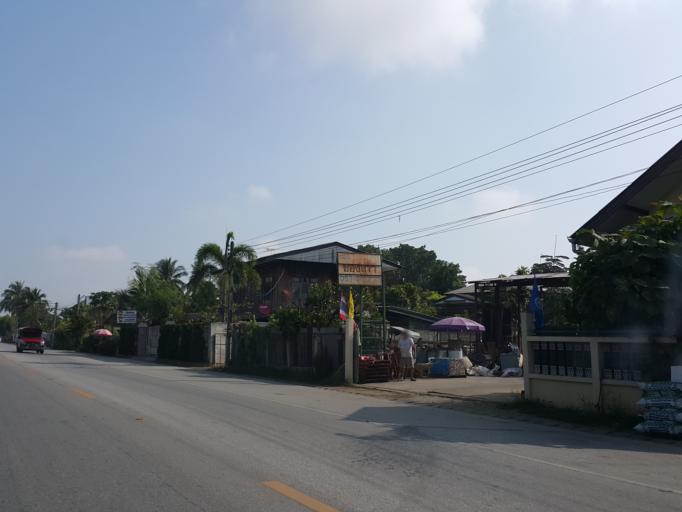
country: TH
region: Chiang Mai
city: San Kamphaeng
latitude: 18.7904
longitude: 99.1009
